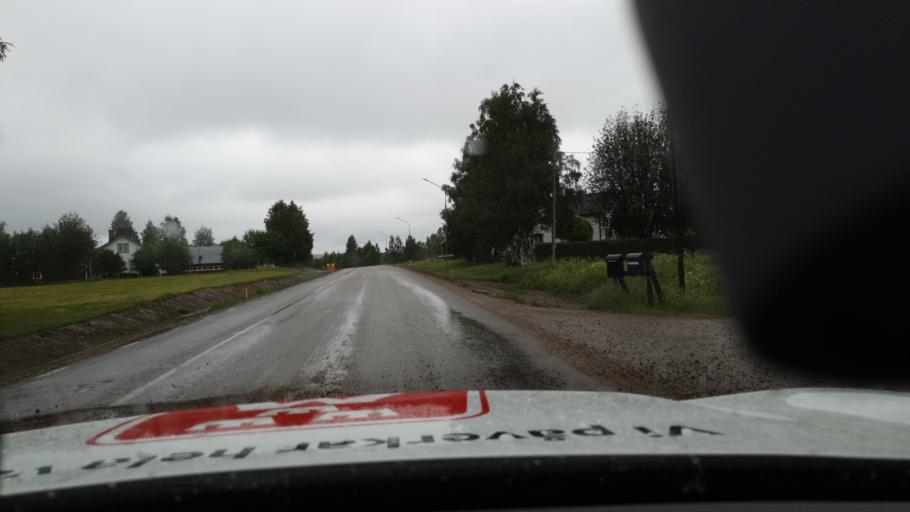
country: FI
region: Lapland
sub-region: Torniolaakso
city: Pello
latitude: 66.5619
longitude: 23.8410
